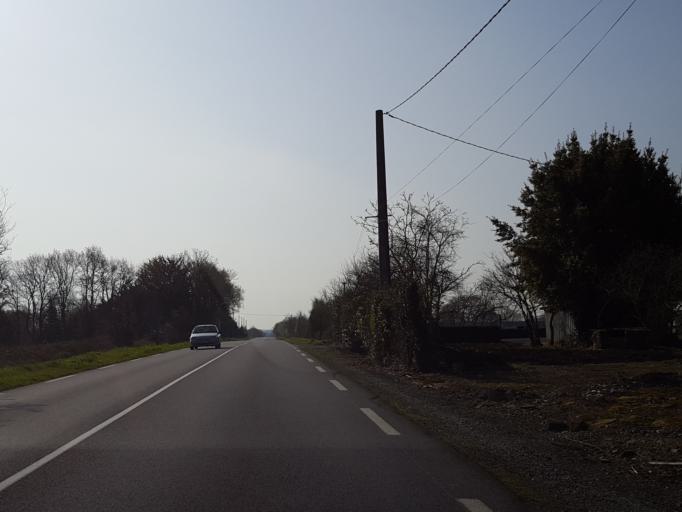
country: FR
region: Pays de la Loire
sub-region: Departement de la Vendee
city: Rocheserviere
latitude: 46.9310
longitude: -1.5123
